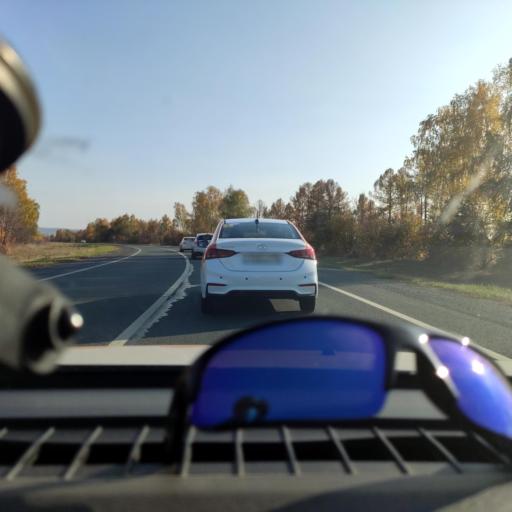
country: RU
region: Samara
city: Bereza
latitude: 53.4775
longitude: 50.1166
